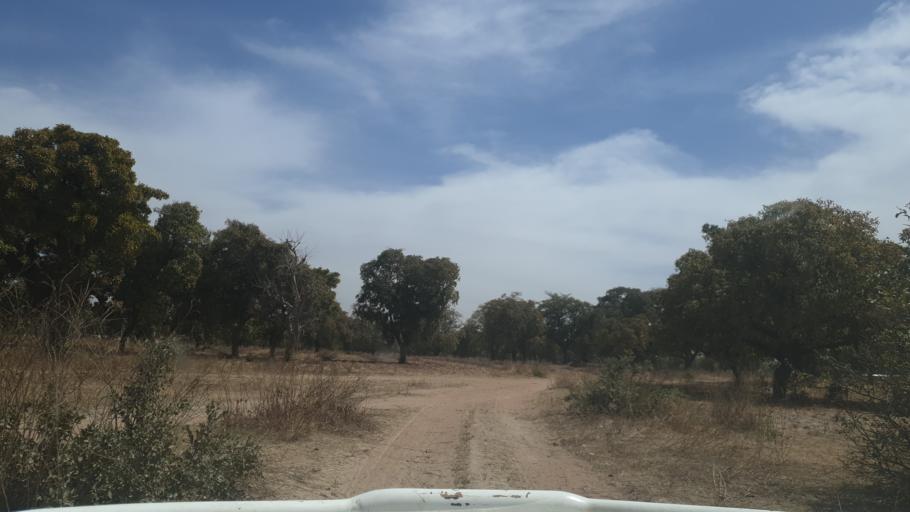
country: ML
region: Sikasso
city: Yorosso
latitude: 12.2923
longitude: -4.6616
